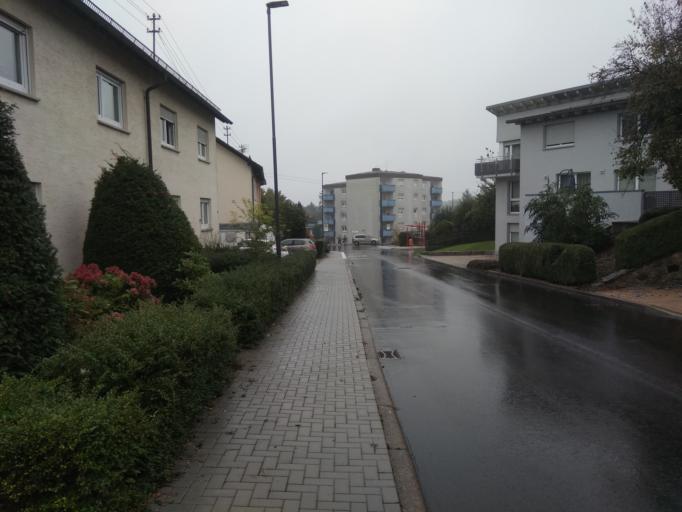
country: DE
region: Baden-Wuerttemberg
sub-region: Karlsruhe Region
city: Mosbach
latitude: 49.3486
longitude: 9.1697
